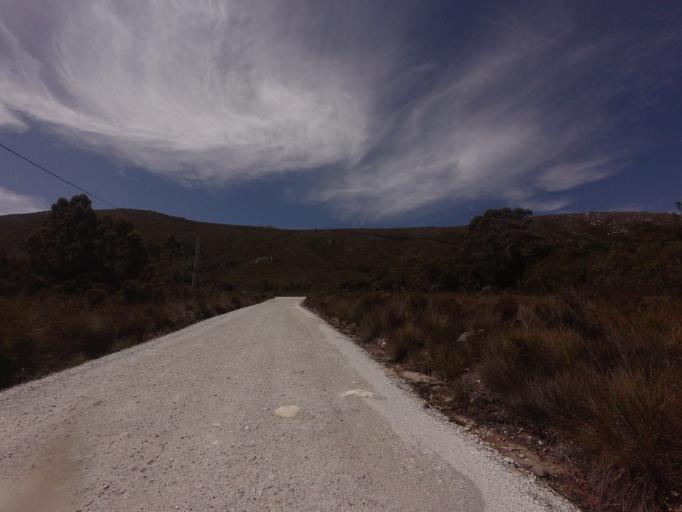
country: AU
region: Tasmania
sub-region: West Coast
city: Queenstown
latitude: -42.7868
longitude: 146.0613
